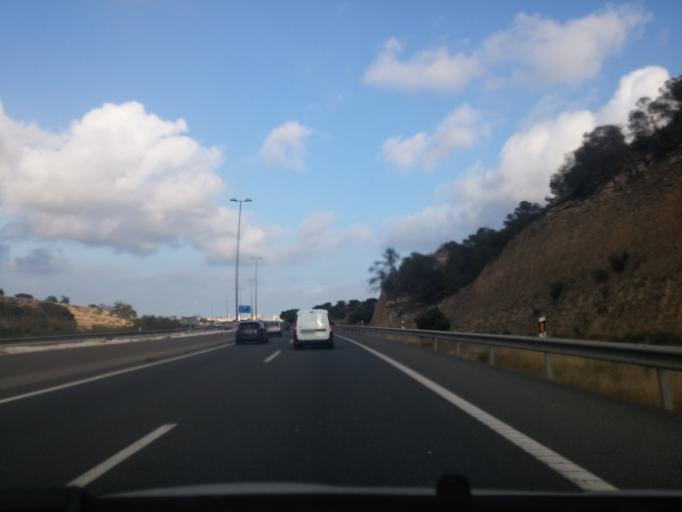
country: ES
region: Valencia
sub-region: Provincia de Alicante
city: Alicante
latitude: 38.3802
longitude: -0.4699
